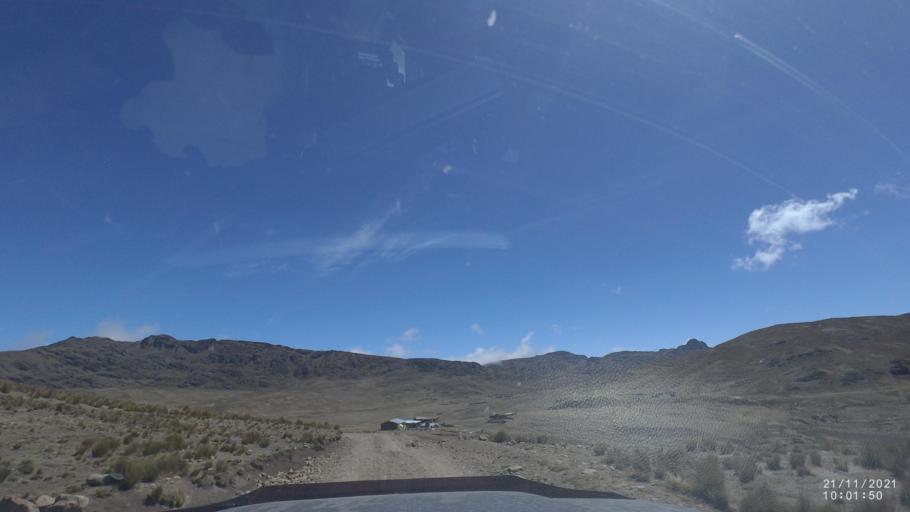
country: BO
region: Cochabamba
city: Cochabamba
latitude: -17.0316
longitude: -66.2753
